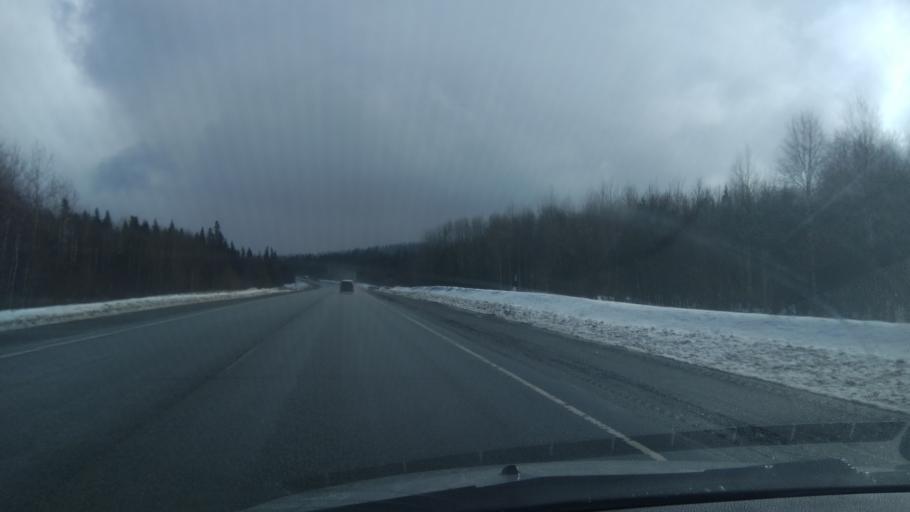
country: RU
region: Sverdlovsk
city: Arti
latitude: 56.7912
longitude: 58.4975
